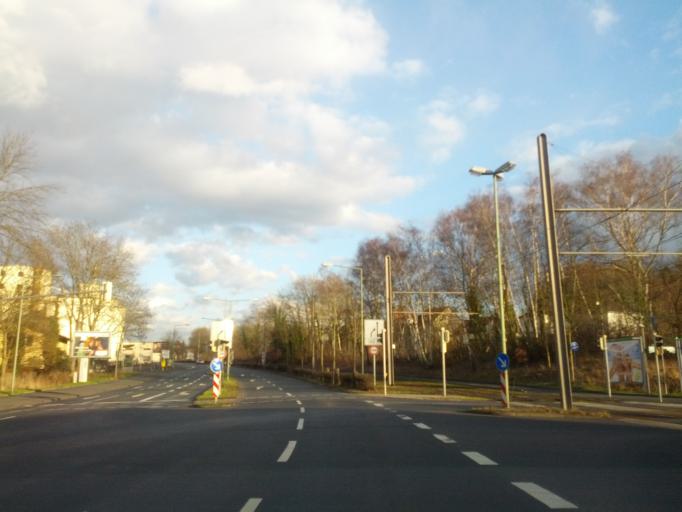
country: DE
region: Hesse
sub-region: Regierungsbezirk Kassel
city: Lohfelden
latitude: 51.2951
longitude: 9.5464
